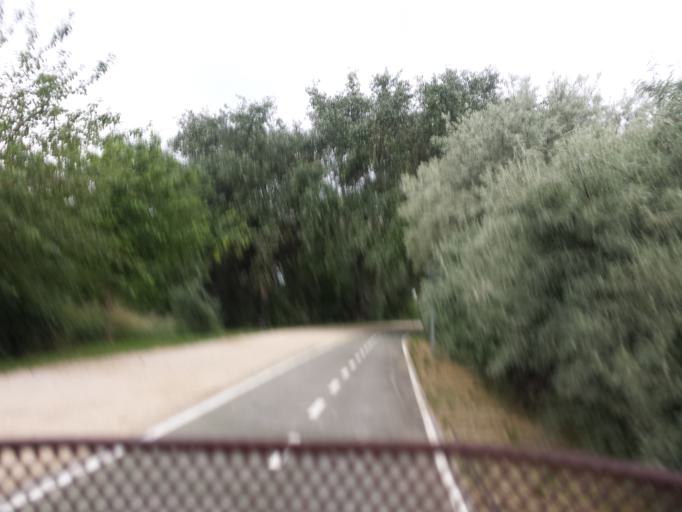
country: ES
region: Aragon
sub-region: Provincia de Zaragoza
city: Almozara
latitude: 41.6787
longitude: -0.9024
